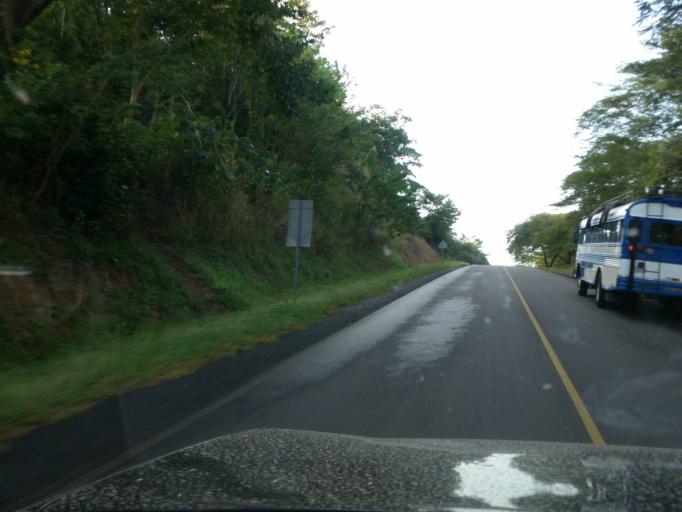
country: NI
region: Rio San Juan
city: San Miguelito
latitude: 11.3769
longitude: -84.7827
